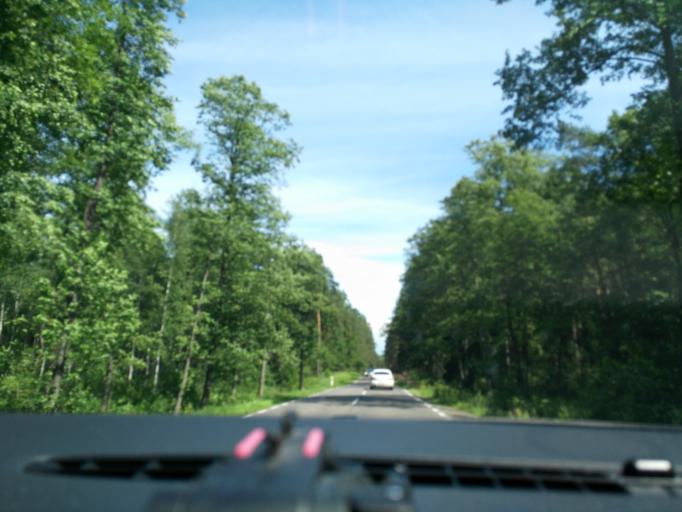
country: PL
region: Podlasie
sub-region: Powiat augustowski
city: Augustow
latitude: 53.8471
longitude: 23.0308
